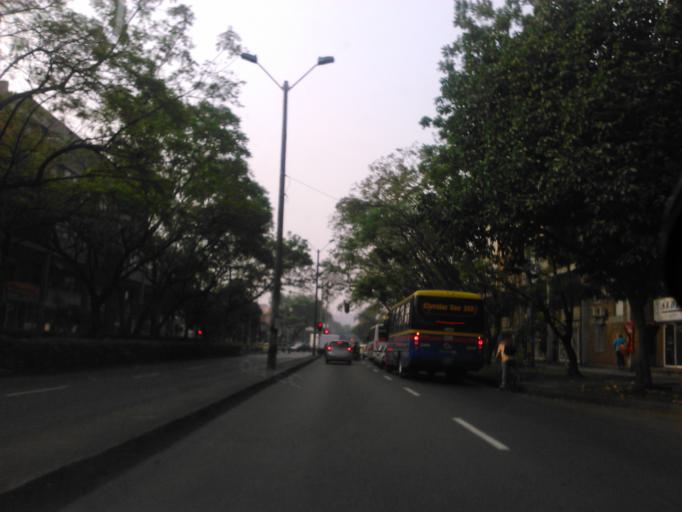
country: CO
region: Antioquia
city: Medellin
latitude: 6.2350
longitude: -75.6023
